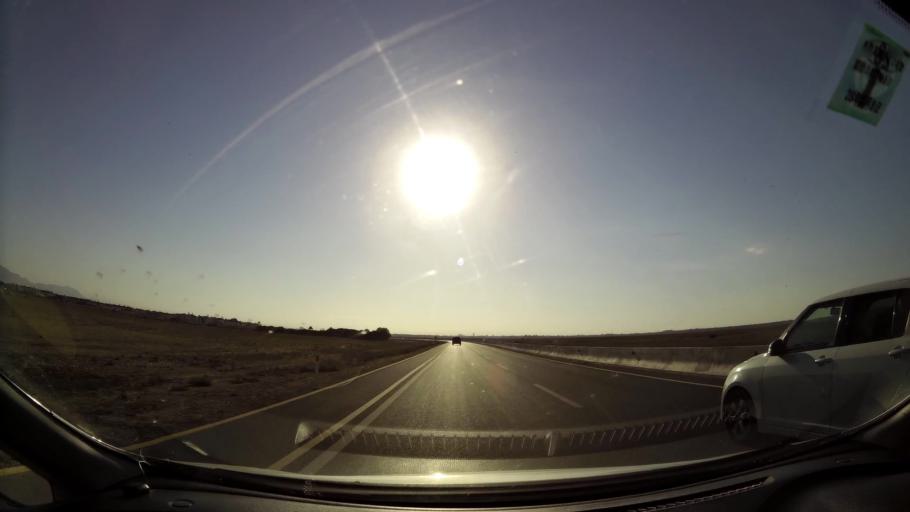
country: CY
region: Lefkosia
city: Nicosia
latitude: 35.2005
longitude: 33.2880
